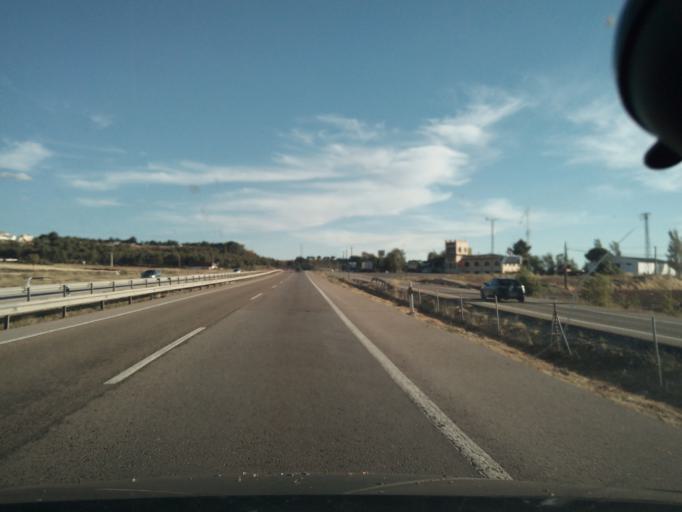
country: ES
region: Castille-La Mancha
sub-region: Province of Toledo
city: Dosbarrios
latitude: 39.7980
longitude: -3.4800
